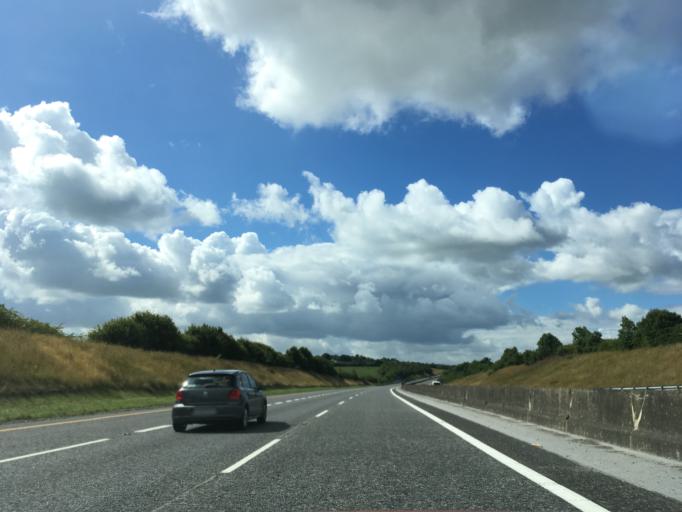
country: IE
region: Munster
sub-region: County Cork
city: Rathcormac
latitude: 52.0524
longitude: -8.3066
